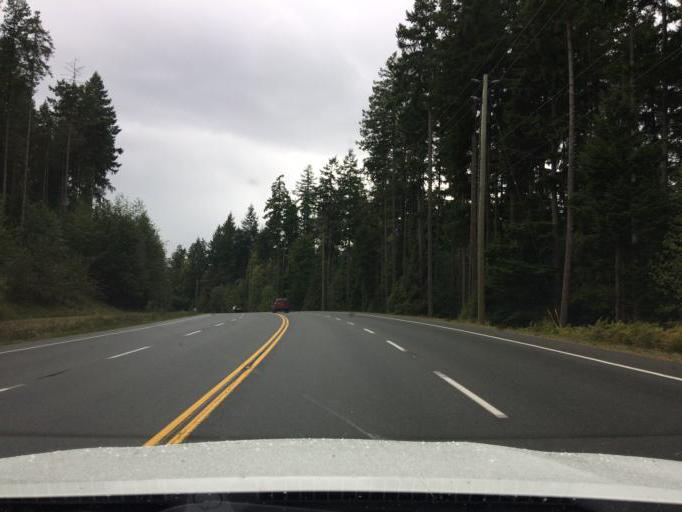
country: CA
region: British Columbia
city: Courtenay
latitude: 49.7195
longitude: -124.9802
